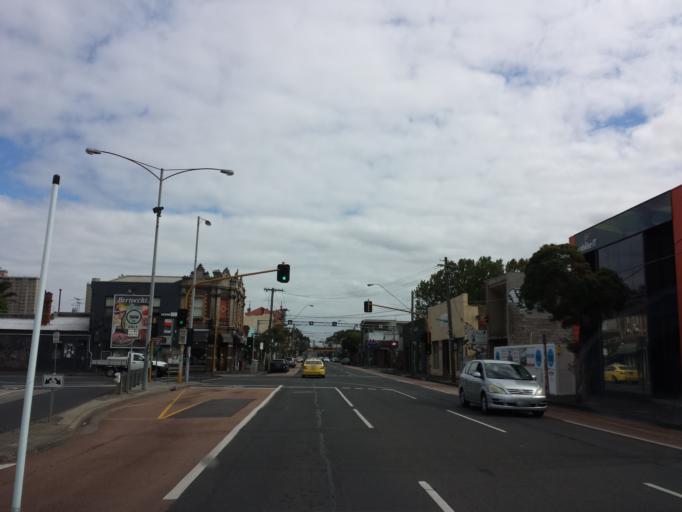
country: AU
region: Victoria
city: Abbotsford
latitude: -37.8004
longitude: 144.9982
